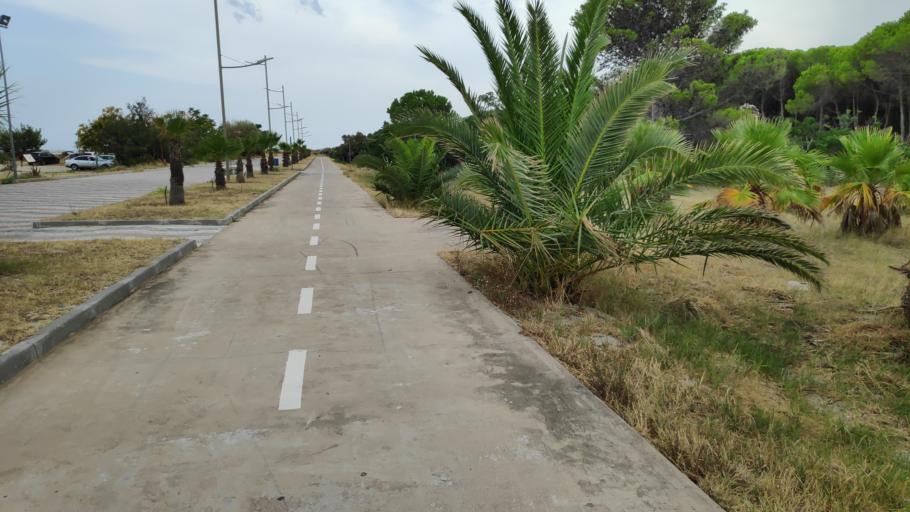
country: IT
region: Calabria
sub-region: Provincia di Catanzaro
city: Soverato Marina
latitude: 38.6829
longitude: 16.5571
